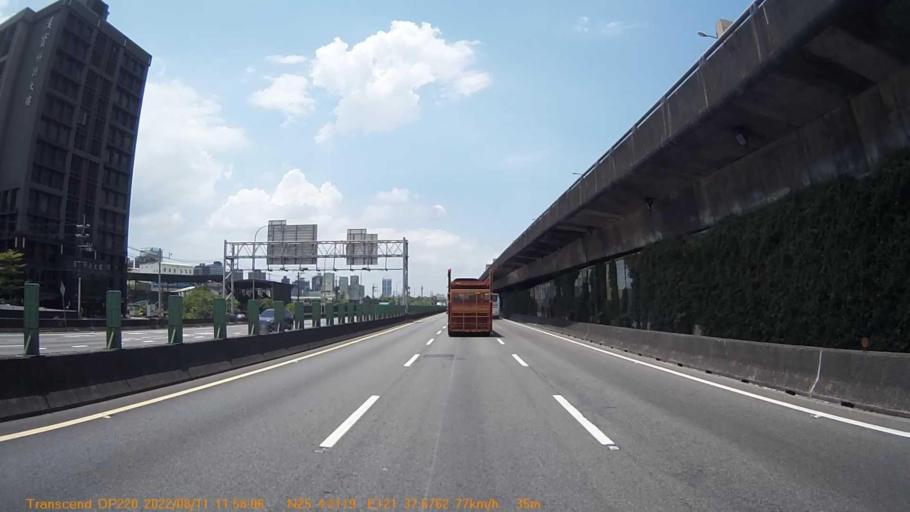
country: TW
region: Taipei
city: Taipei
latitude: 25.0677
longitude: 121.6275
